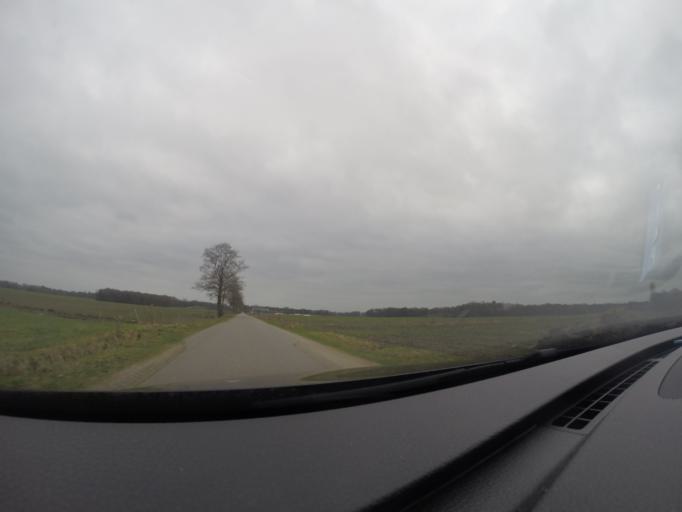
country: NL
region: Overijssel
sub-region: Gemeente Haaksbergen
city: Haaksbergen
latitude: 52.1193
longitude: 6.7352
